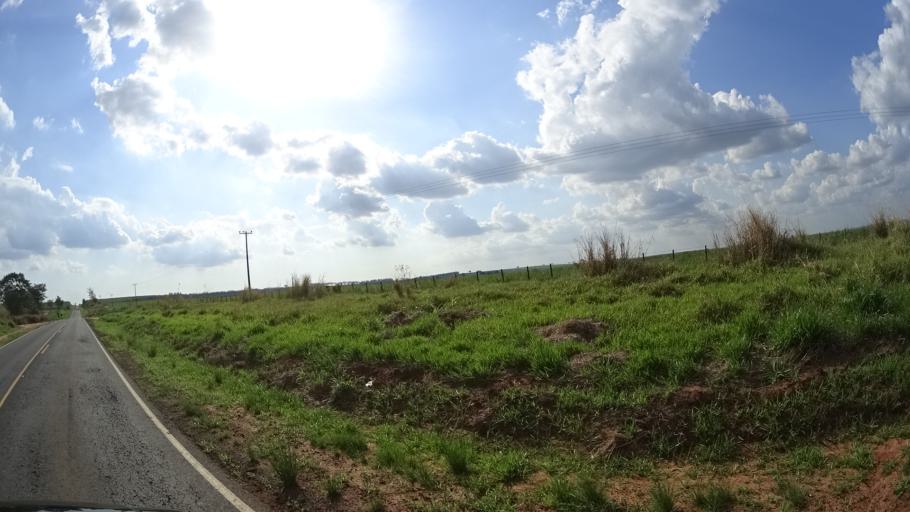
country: BR
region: Sao Paulo
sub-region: Urupes
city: Urupes
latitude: -21.2053
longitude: -49.3298
